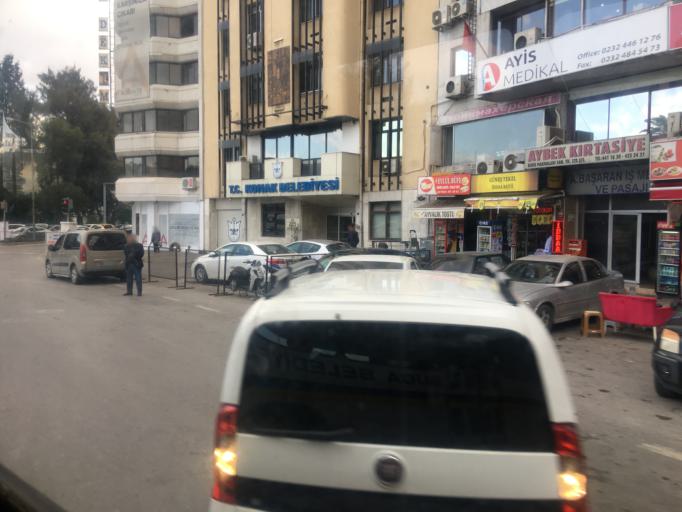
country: TR
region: Izmir
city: Izmir
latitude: 38.4234
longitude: 27.1433
